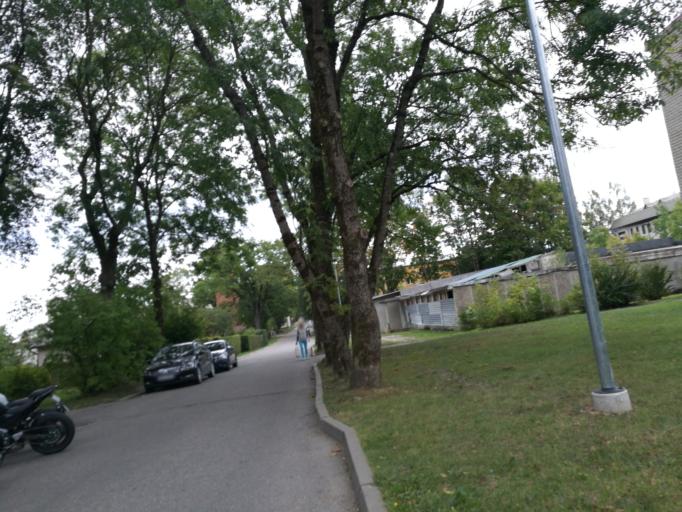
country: LV
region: Limbazu Rajons
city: Limbazi
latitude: 57.5125
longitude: 24.7175
